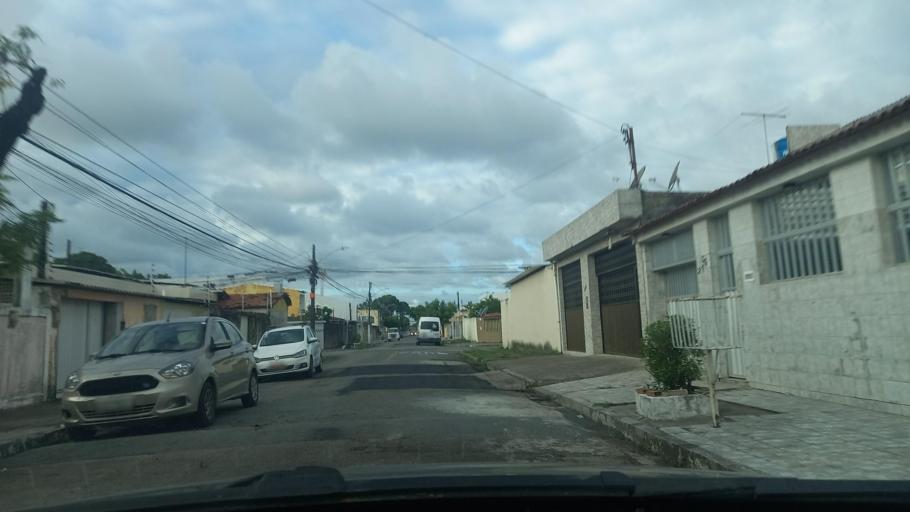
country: BR
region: Pernambuco
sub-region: Recife
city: Recife
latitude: -8.1108
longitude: -34.9228
